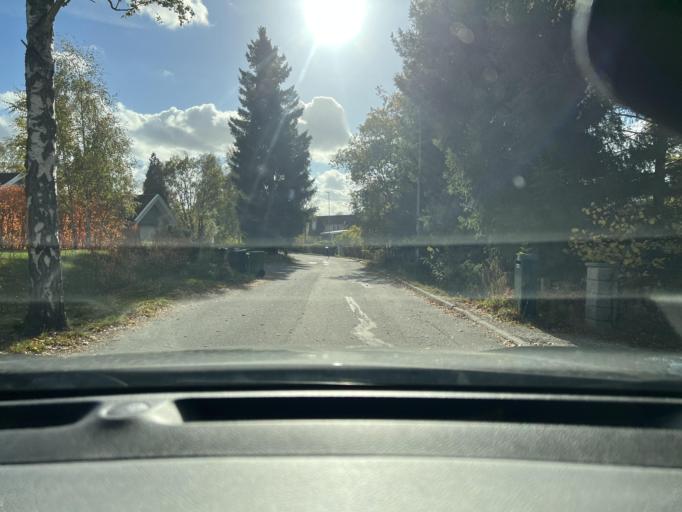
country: SE
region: Stockholm
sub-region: Vallentuna Kommun
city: Vallentuna
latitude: 59.5021
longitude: 18.0823
